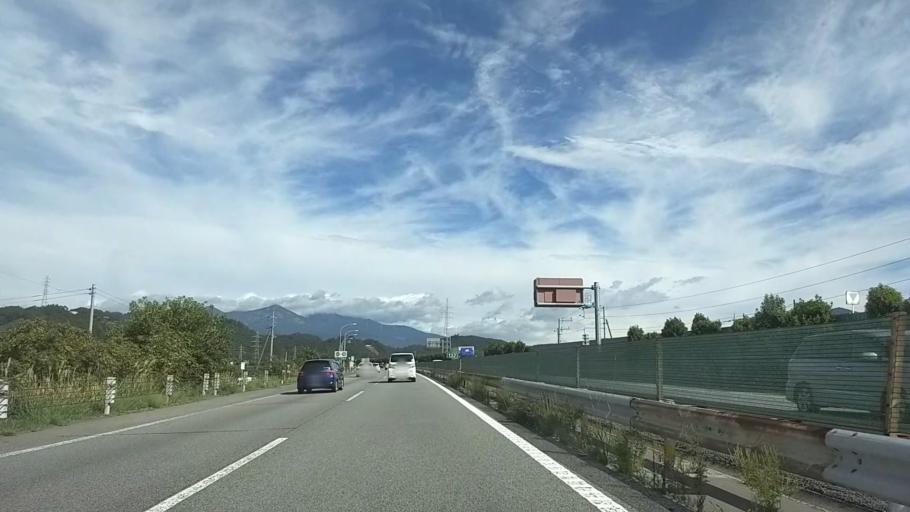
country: JP
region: Yamanashi
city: Nirasaki
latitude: 35.7774
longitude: 138.4225
